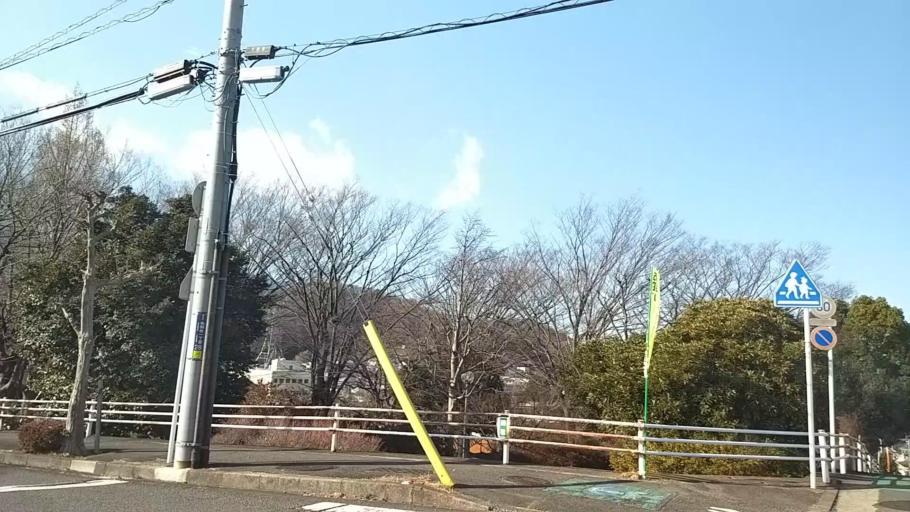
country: JP
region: Kanagawa
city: Atsugi
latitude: 35.4398
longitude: 139.3290
